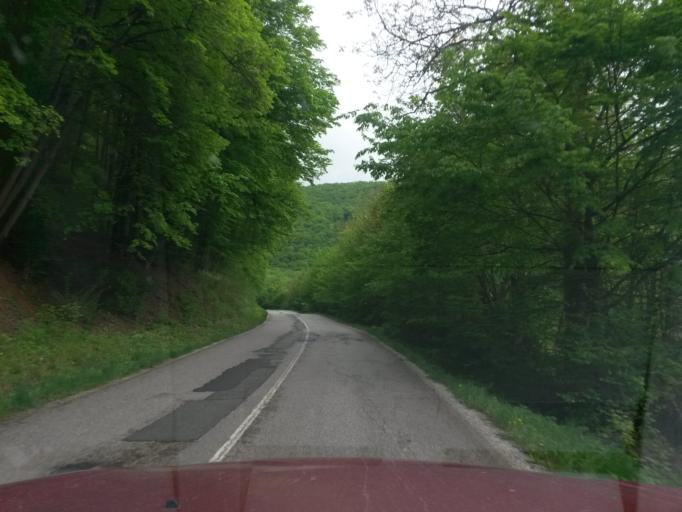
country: SK
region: Kosicky
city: Roznava
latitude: 48.5668
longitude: 20.4674
